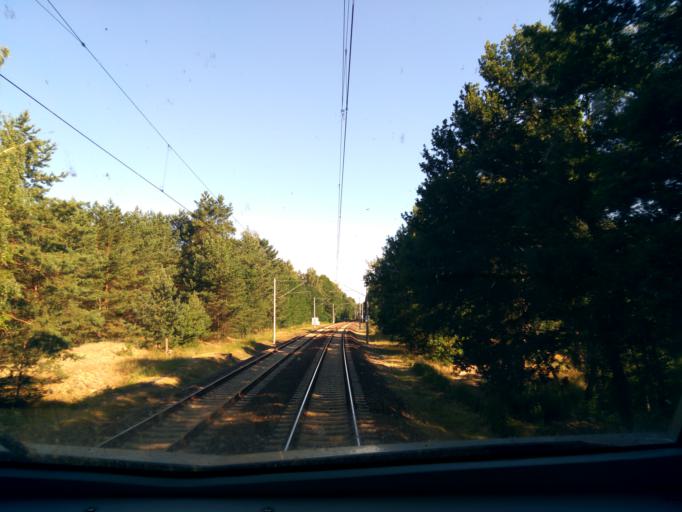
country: DE
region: Brandenburg
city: Schwerin
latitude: 52.1758
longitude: 13.6410
